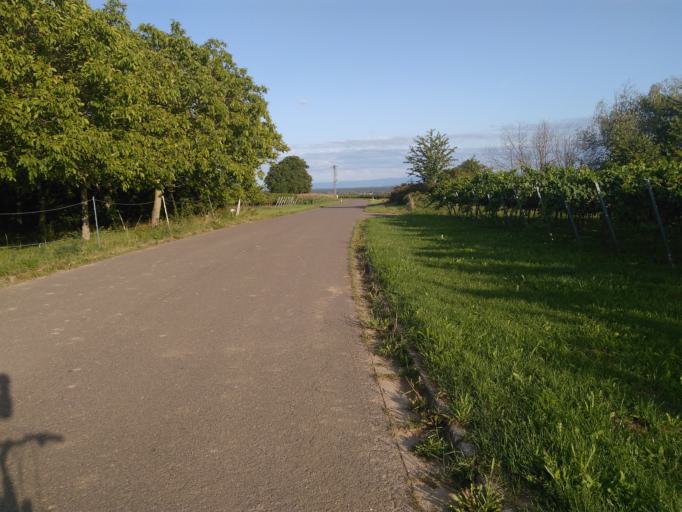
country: DE
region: Rheinland-Pfalz
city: Oberotterbach
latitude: 49.0579
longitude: 7.9689
